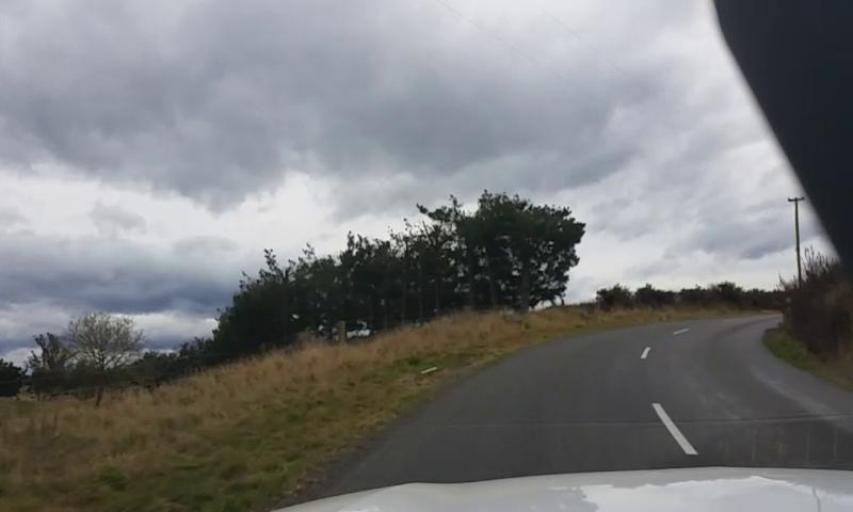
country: NZ
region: Canterbury
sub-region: Waimakariri District
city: Kaiapoi
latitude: -43.2969
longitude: 172.4373
